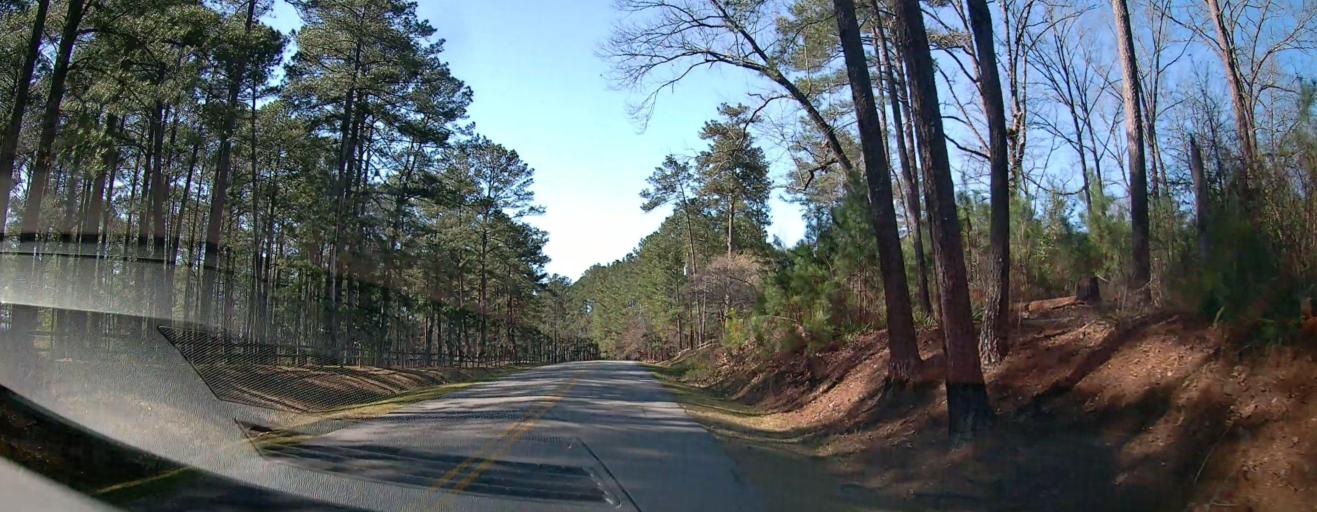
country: US
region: Georgia
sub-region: Butts County
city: Indian Springs
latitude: 33.2505
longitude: -83.9259
